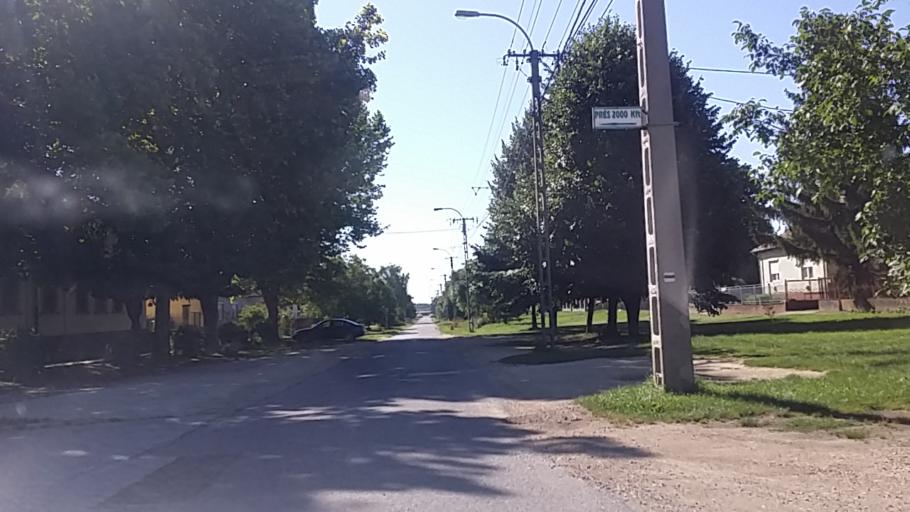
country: HU
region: Fejer
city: Mezofalva
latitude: 46.9306
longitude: 18.7797
